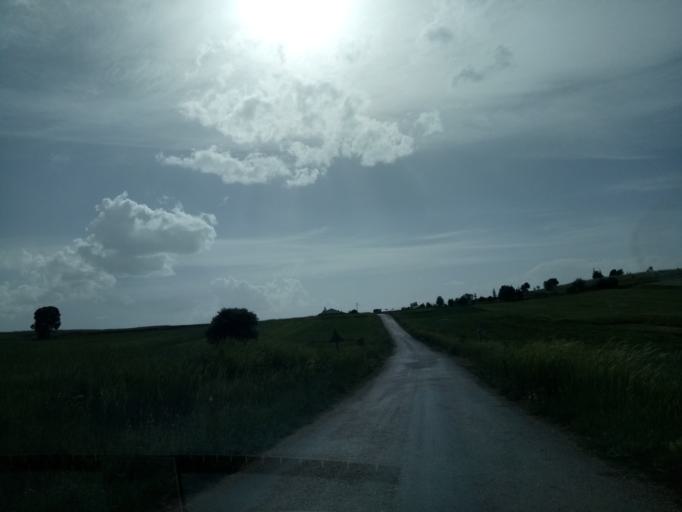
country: TR
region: Konya
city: Ahirli
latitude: 37.2839
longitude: 32.1866
